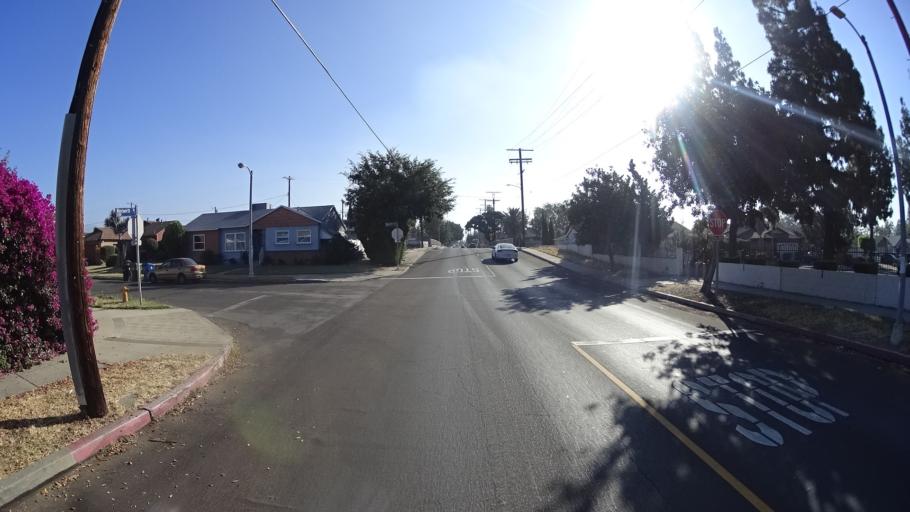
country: US
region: California
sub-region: Los Angeles County
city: Van Nuys
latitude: 34.2315
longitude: -118.4188
